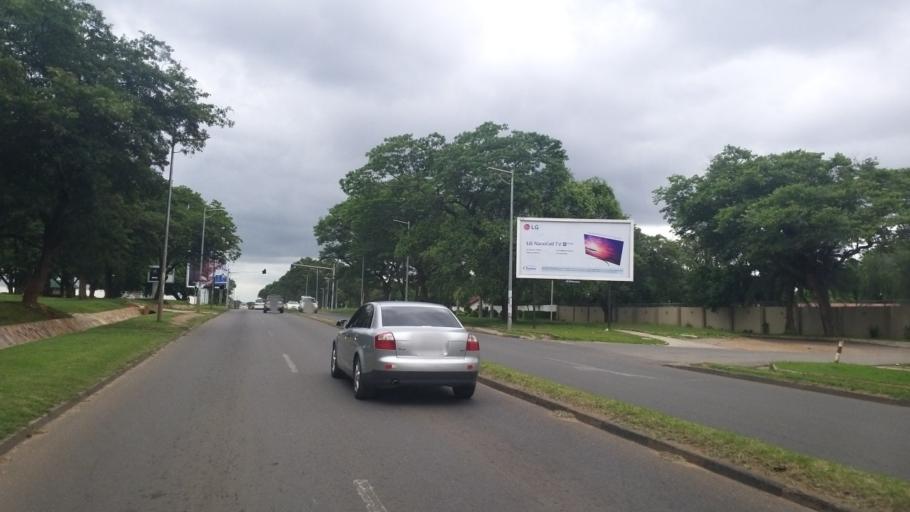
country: ZM
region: Lusaka
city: Lusaka
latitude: -15.4222
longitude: 28.3229
